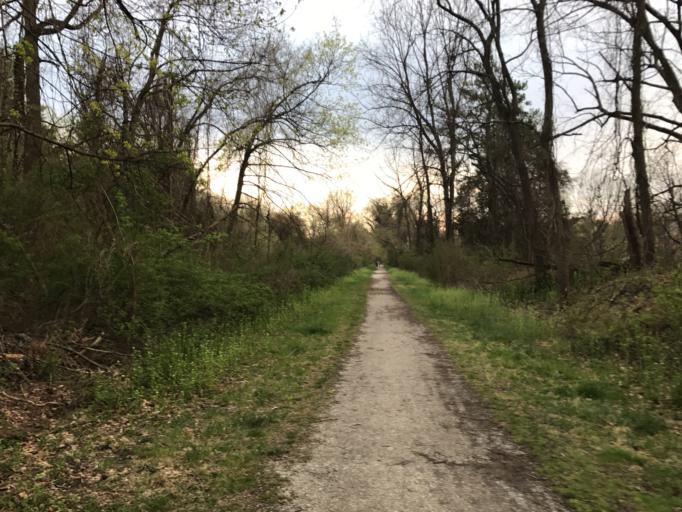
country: US
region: Maryland
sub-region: Baltimore County
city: Hunt Valley
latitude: 39.4998
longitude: -76.6353
